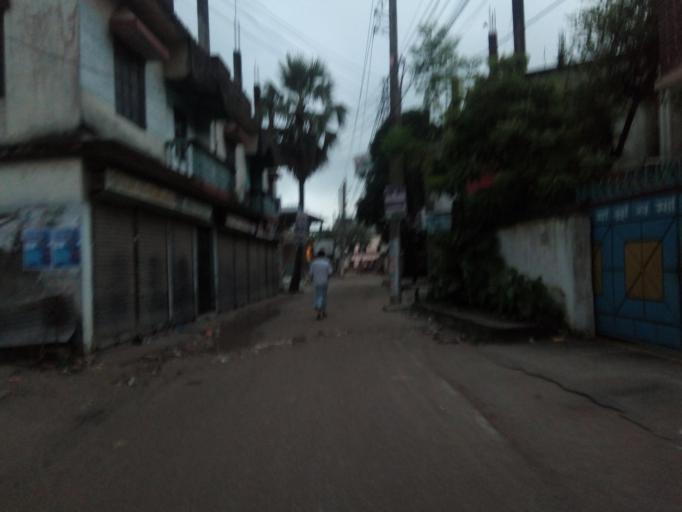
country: BD
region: Dhaka
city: Tungi
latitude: 23.8592
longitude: 90.4274
